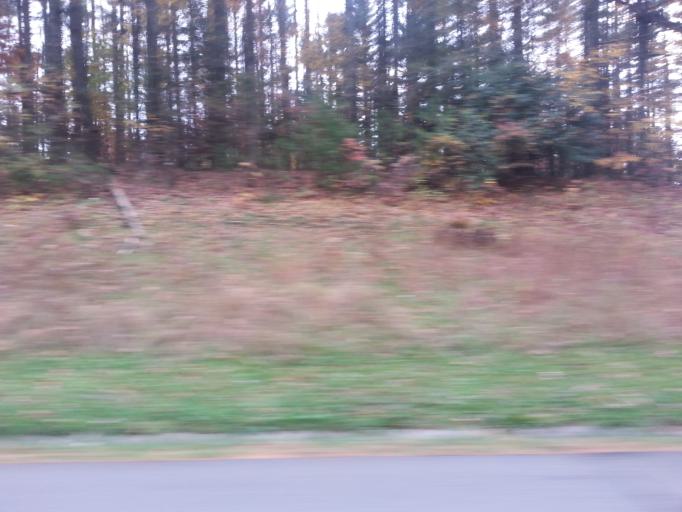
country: US
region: North Carolina
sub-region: Ashe County
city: Jefferson
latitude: 36.3601
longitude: -81.3703
